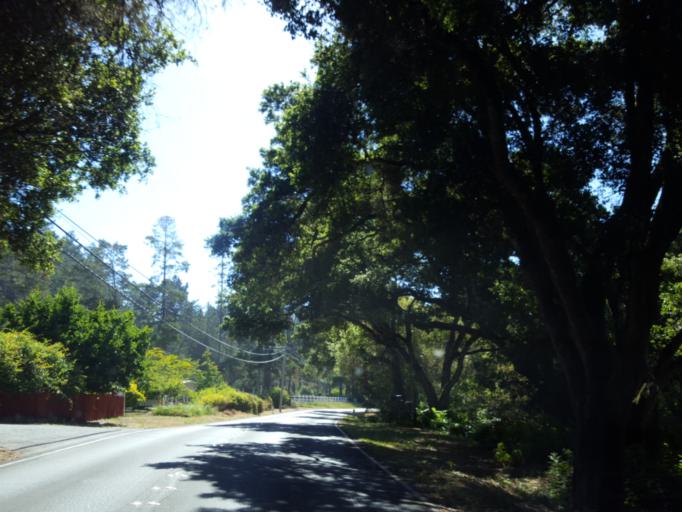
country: US
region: California
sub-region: San Mateo County
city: Portola Valley
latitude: 37.2618
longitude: -122.3357
